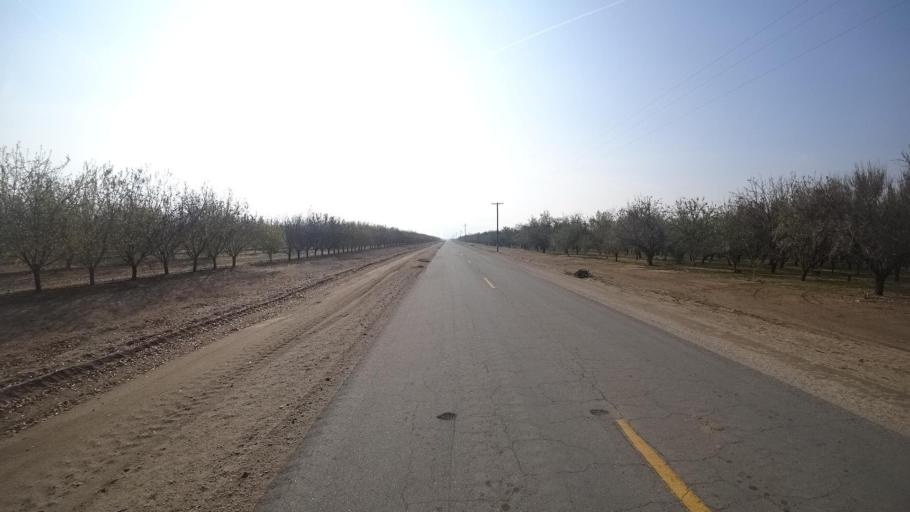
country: US
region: California
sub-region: Kern County
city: Lebec
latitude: 35.0073
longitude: -118.8466
